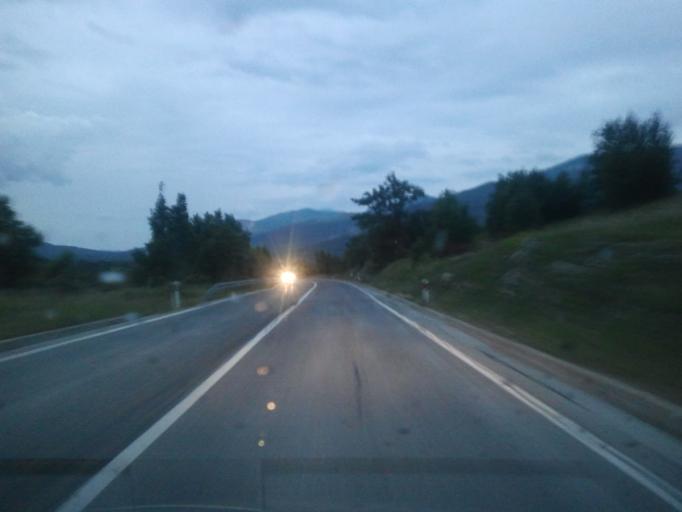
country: HR
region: Zadarska
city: Gracac
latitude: 44.4165
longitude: 15.8888
